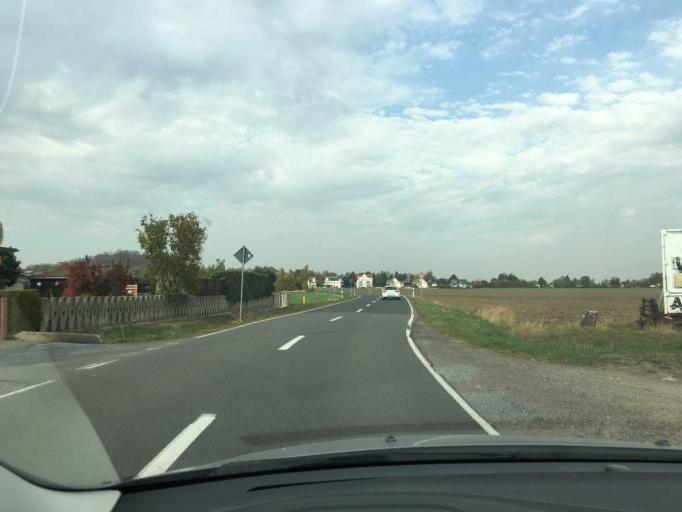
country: DE
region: Saxony-Anhalt
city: Landsberg
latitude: 51.5181
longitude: 12.1690
